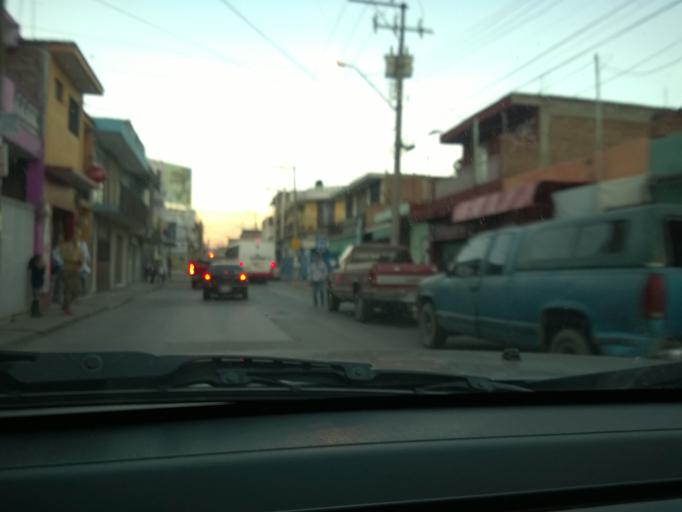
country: MX
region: Guanajuato
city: Leon
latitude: 21.1243
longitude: -101.6637
